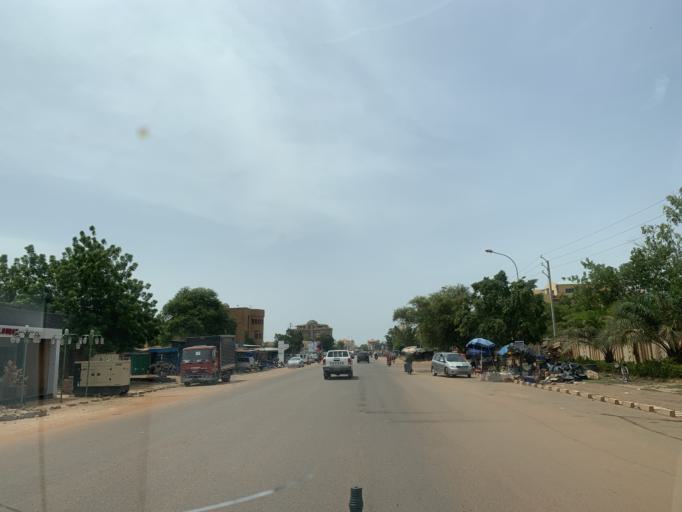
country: BF
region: Centre
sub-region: Kadiogo Province
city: Ouagadougou
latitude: 12.3377
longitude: -1.5020
